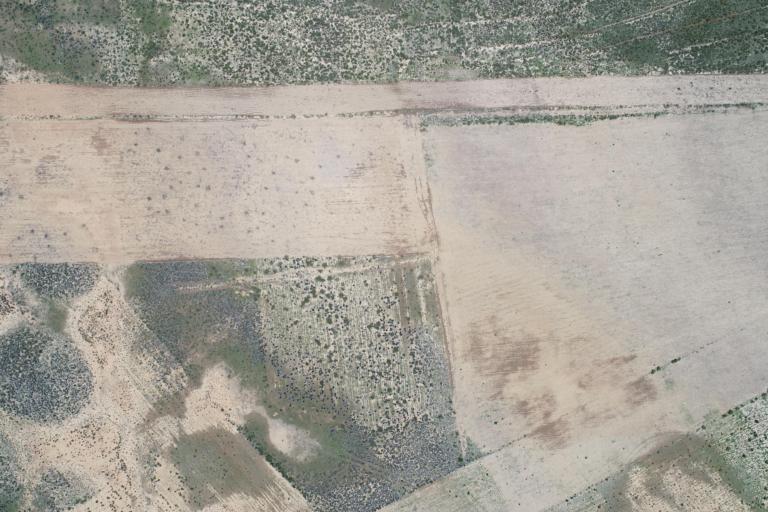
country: BO
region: La Paz
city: Patacamaya
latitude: -17.2826
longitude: -68.5022
